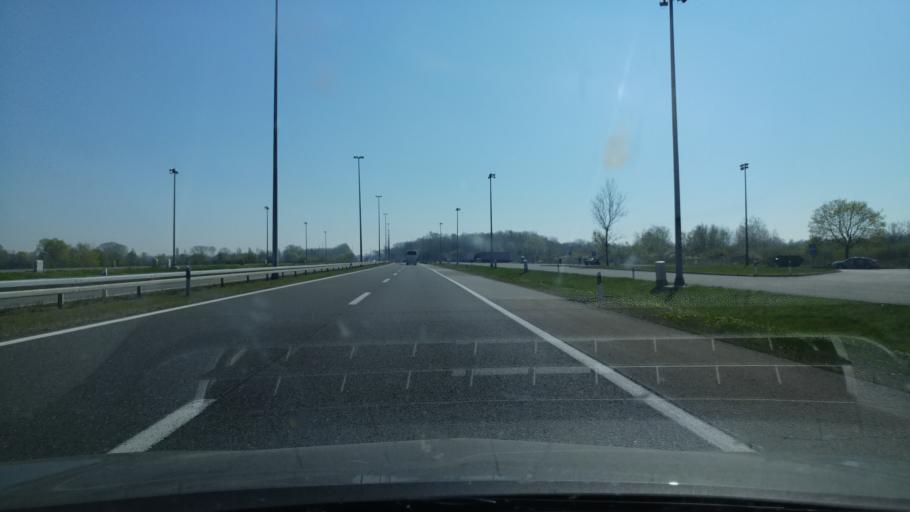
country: HR
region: Brodsko-Posavska
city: Garcin
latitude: 45.1491
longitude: 18.2717
